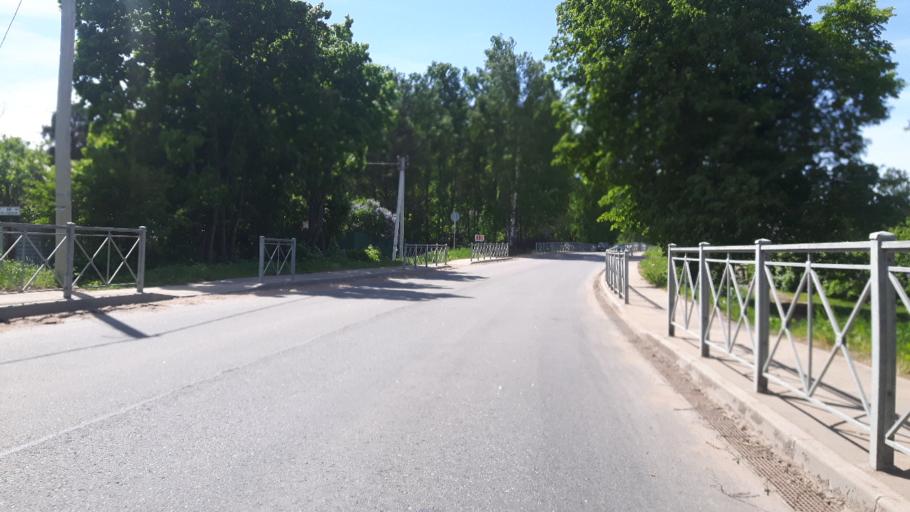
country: RU
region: Leningrad
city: Ust'-Luga
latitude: 59.5834
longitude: 28.1871
